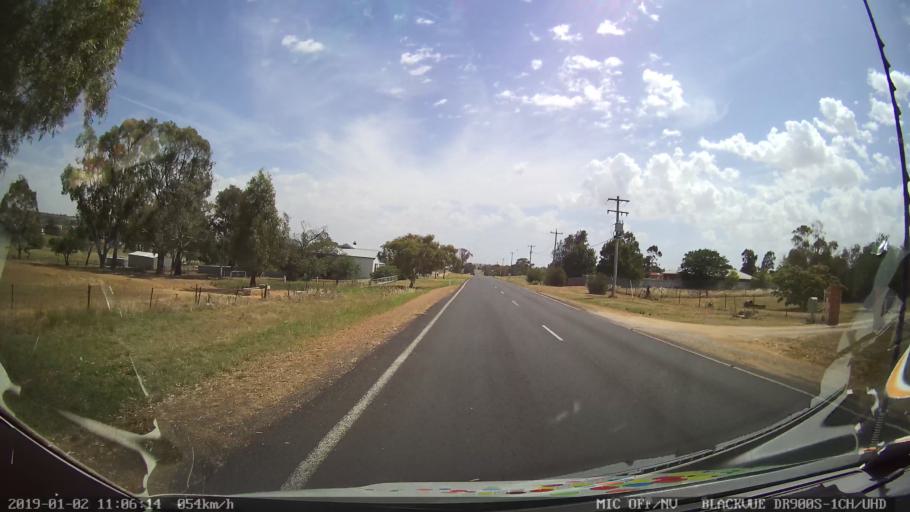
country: AU
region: New South Wales
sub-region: Young
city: Young
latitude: -34.5567
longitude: 148.3559
